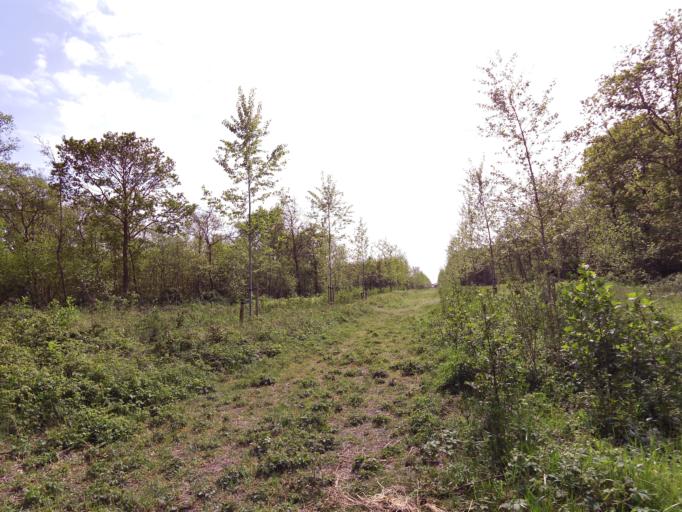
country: NL
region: South Holland
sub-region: Gemeente Goeree-Overflakkee
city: Ouddorp
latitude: 51.7843
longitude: 3.8925
